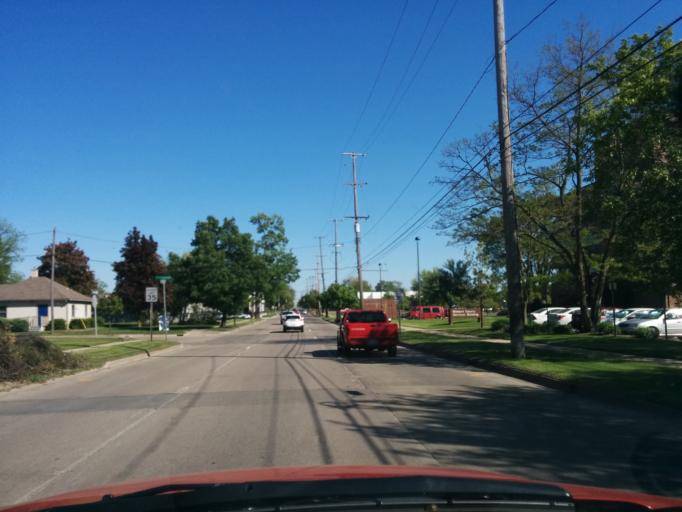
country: US
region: Michigan
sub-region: Midland County
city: Midland
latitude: 43.6166
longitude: -84.2451
